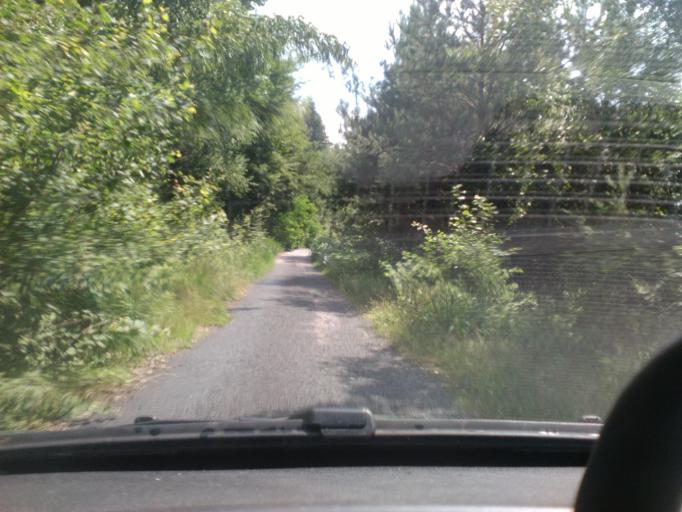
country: FR
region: Lorraine
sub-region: Departement des Vosges
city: Sainte-Marguerite
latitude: 48.2994
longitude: 6.9903
